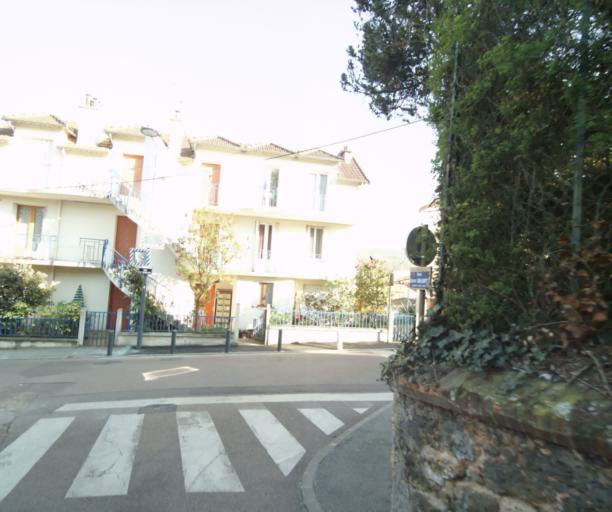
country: FR
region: Ile-de-France
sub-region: Departement des Hauts-de-Seine
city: Ville-d'Avray
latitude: 48.8193
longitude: 2.1955
